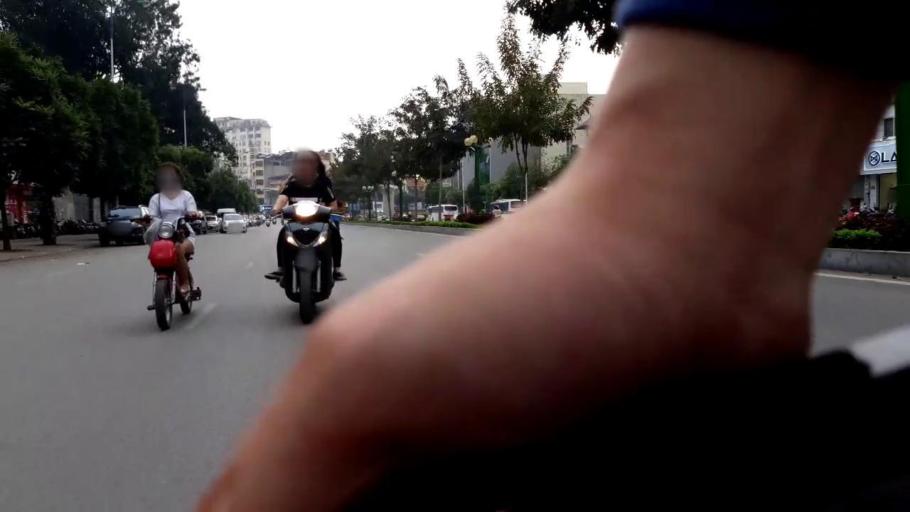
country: VN
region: Ha Noi
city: Cau Giay
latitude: 21.0358
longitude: 105.7978
